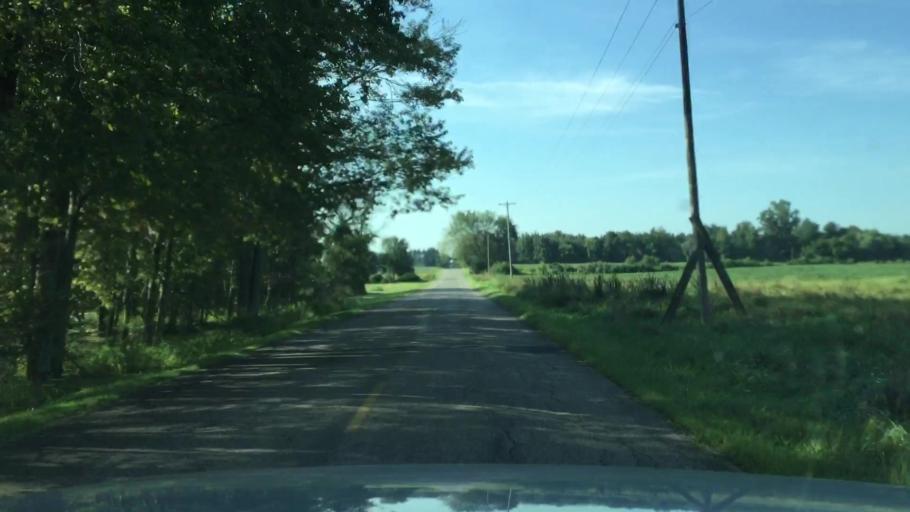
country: US
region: Michigan
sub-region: Lenawee County
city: Hudson
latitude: 41.9060
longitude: -84.4204
